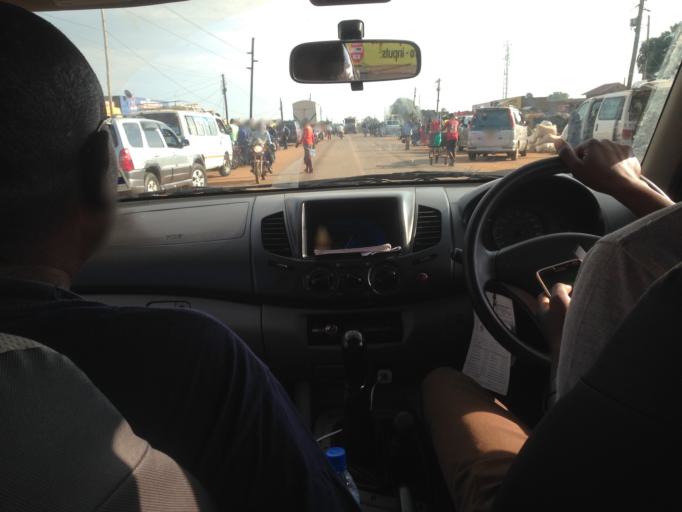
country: UG
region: Western Region
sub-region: Kiryandongo District
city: Kiryandongo
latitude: 1.9530
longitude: 32.1409
